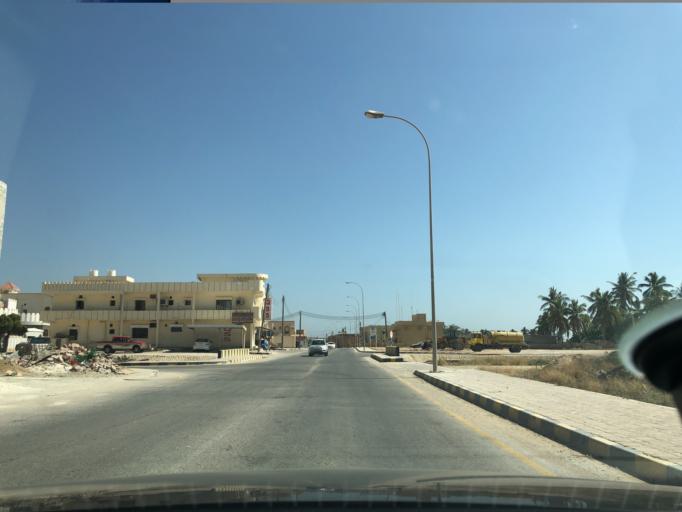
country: OM
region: Zufar
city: Salalah
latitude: 17.0387
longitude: 54.3908
